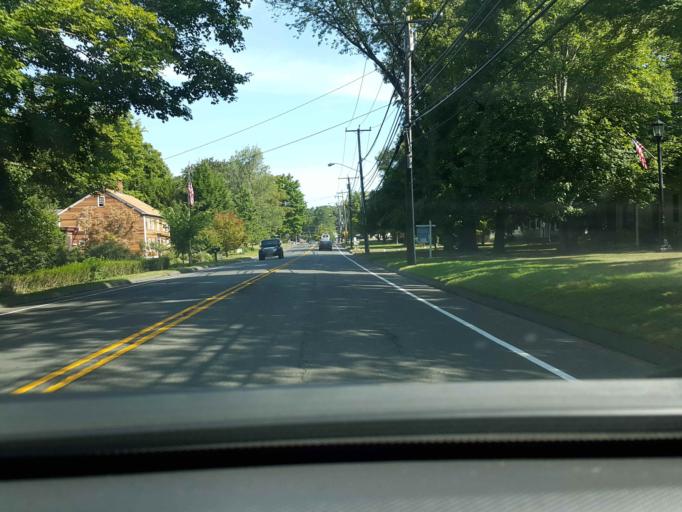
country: US
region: Connecticut
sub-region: Middlesex County
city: Durham
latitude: 41.4817
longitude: -72.6817
